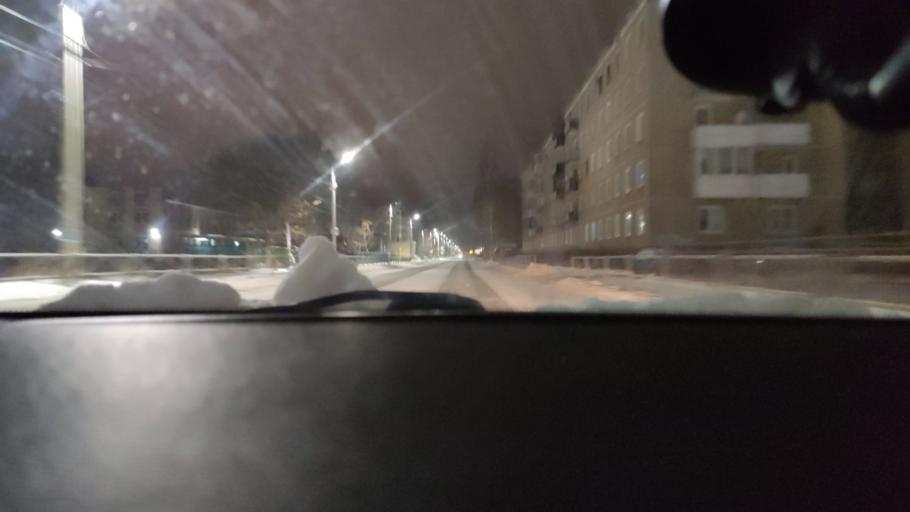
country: RU
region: Perm
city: Krasnokamsk
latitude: 58.0873
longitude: 55.7544
